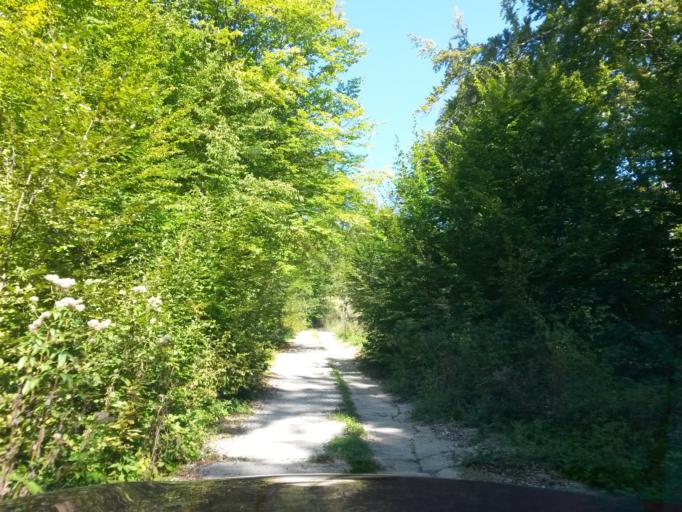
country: SK
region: Presovsky
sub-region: Okres Presov
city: Presov
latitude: 48.9712
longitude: 21.1469
